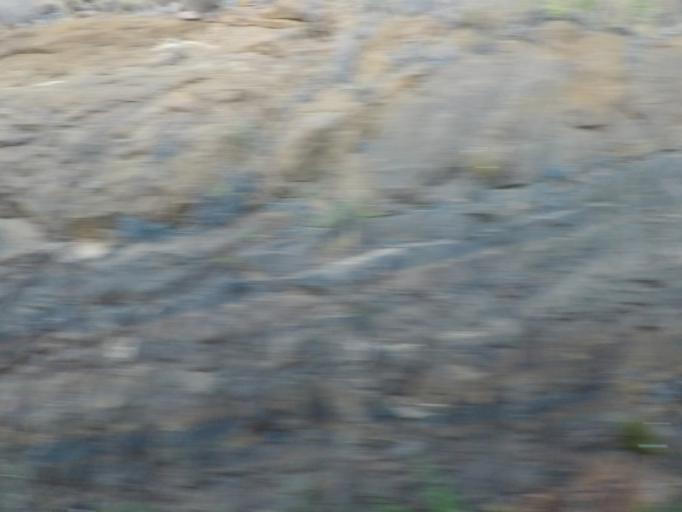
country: ES
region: Canary Islands
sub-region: Provincia de Santa Cruz de Tenerife
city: Alajero
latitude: 28.0566
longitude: -17.2017
